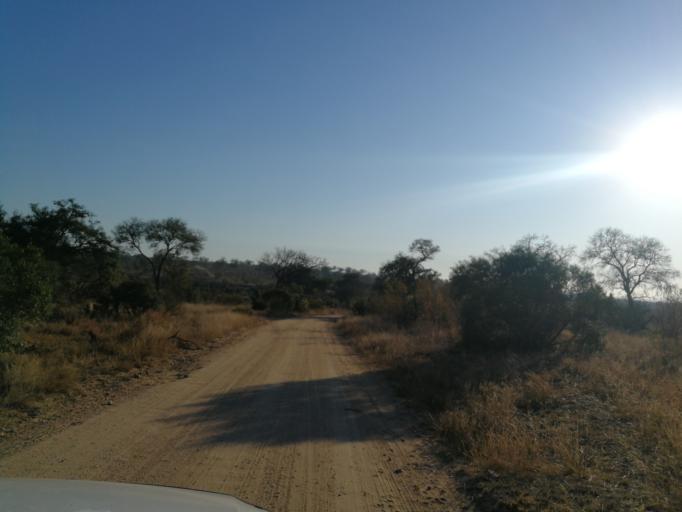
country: ZA
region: Limpopo
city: Thulamahashi
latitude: -25.0125
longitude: 31.4294
